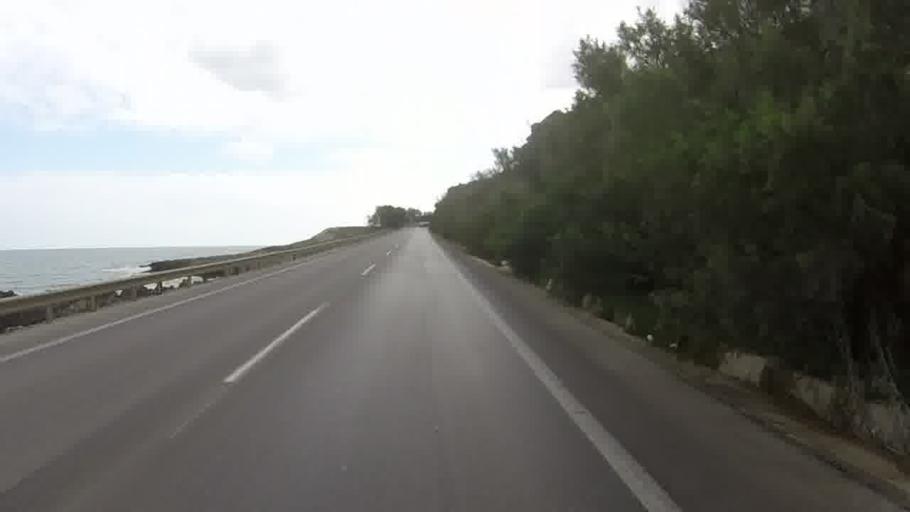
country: GR
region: Crete
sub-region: Nomos Rethymnis
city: Atsipopoulon
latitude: 35.3628
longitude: 24.3980
